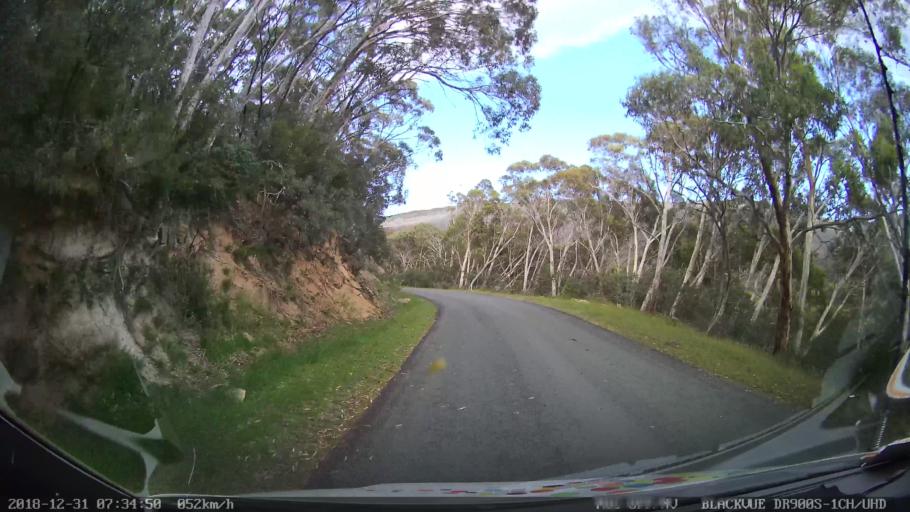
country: AU
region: New South Wales
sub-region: Snowy River
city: Jindabyne
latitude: -36.3321
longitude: 148.4487
